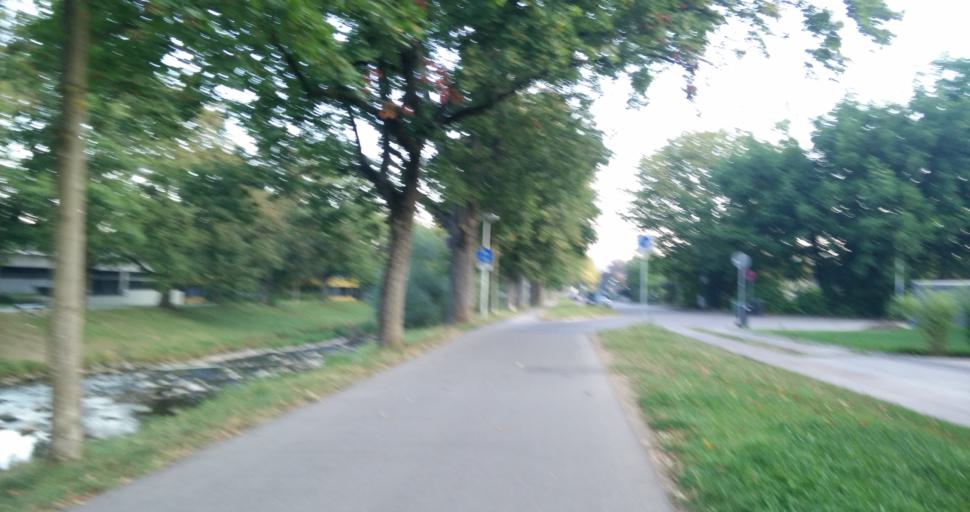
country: DE
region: Baden-Wuerttemberg
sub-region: Tuebingen Region
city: Tuebingen
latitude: 48.5055
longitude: 9.0577
